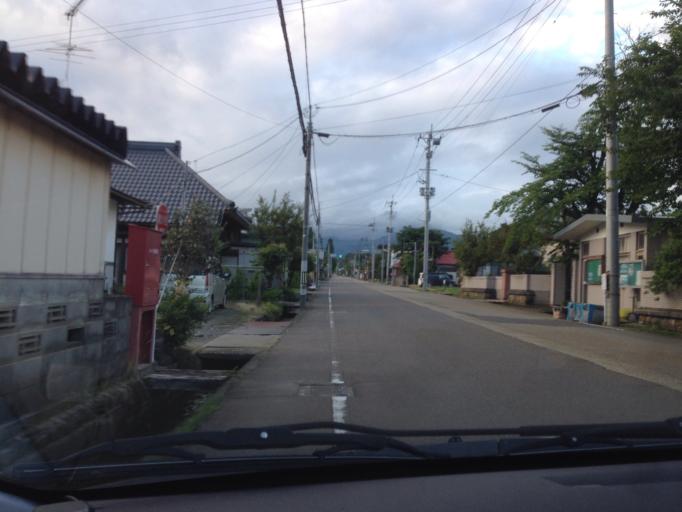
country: JP
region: Fukushima
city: Kitakata
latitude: 37.6843
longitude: 139.8636
